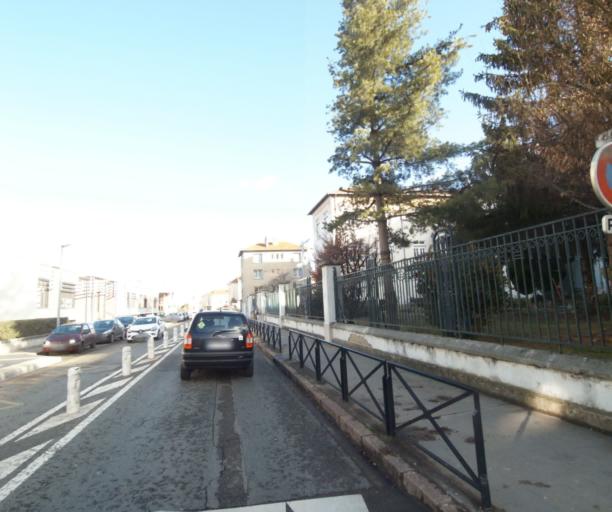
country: FR
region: Rhone-Alpes
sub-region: Departement de la Loire
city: Roanne
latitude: 46.0441
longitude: 4.0741
